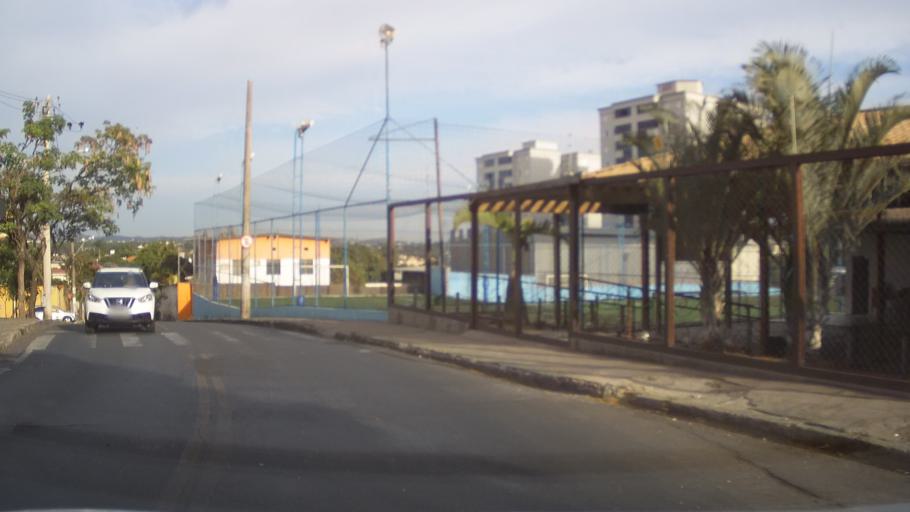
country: BR
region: Minas Gerais
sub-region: Belo Horizonte
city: Belo Horizonte
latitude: -19.8715
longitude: -43.9899
